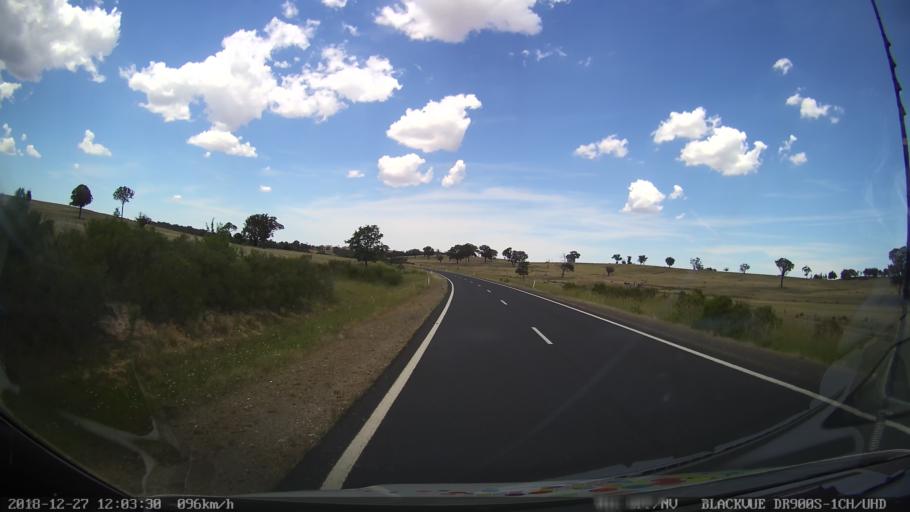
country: AU
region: New South Wales
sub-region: Blayney
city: Blayney
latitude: -33.7859
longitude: 149.3582
